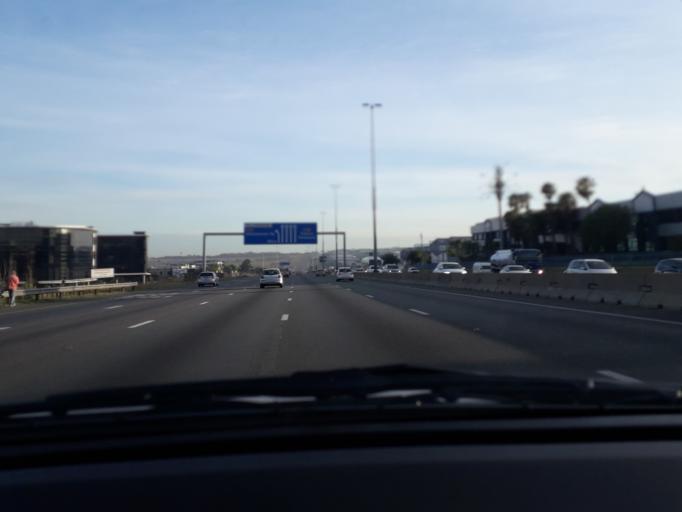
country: ZA
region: Gauteng
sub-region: City of Johannesburg Metropolitan Municipality
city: Midrand
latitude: -25.9640
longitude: 28.1312
